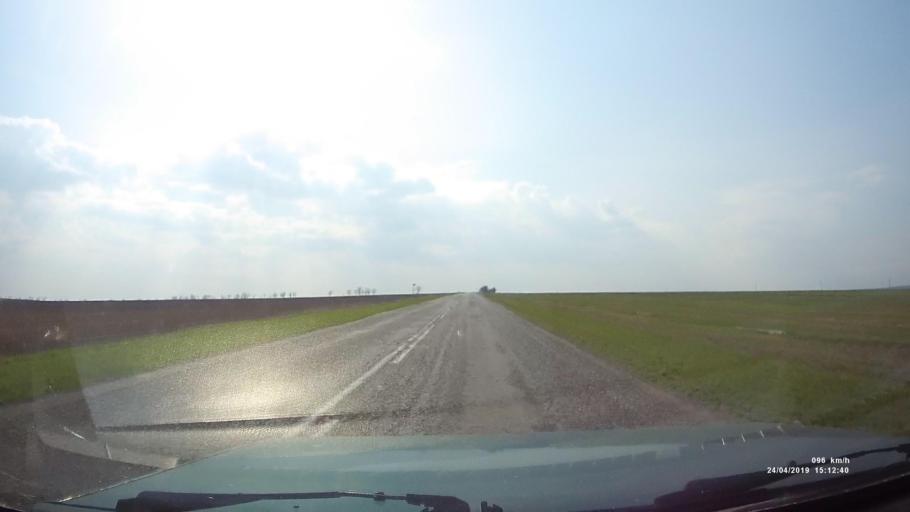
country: RU
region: Rostov
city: Remontnoye
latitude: 46.5464
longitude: 43.2955
